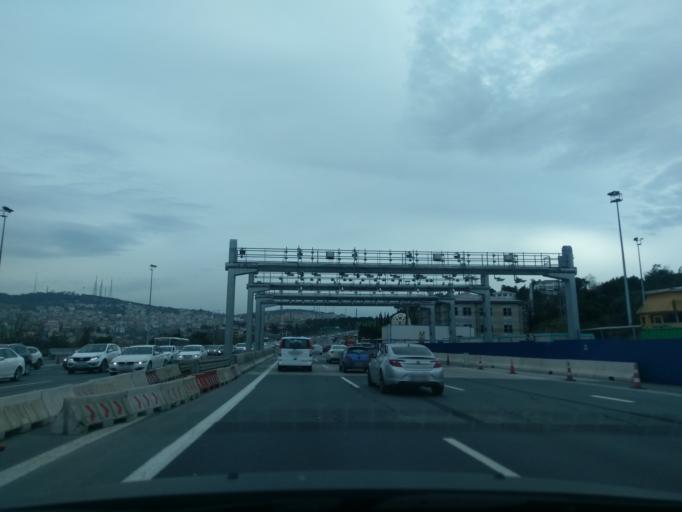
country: TR
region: Istanbul
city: UEskuedar
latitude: 41.0394
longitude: 29.0407
